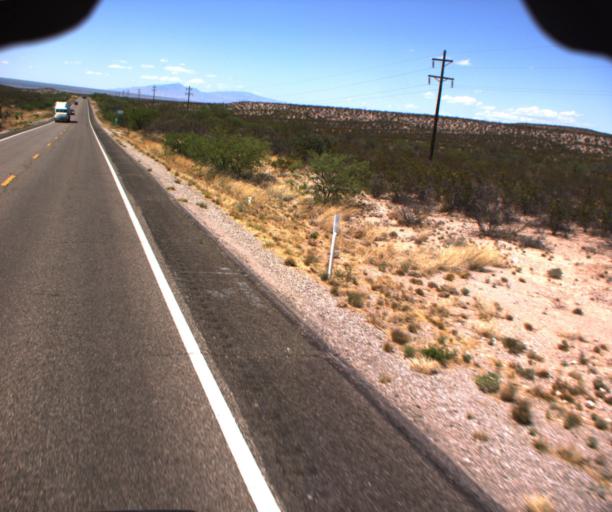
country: US
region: Arizona
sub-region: Cochise County
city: Tombstone
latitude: 31.7768
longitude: -110.1326
